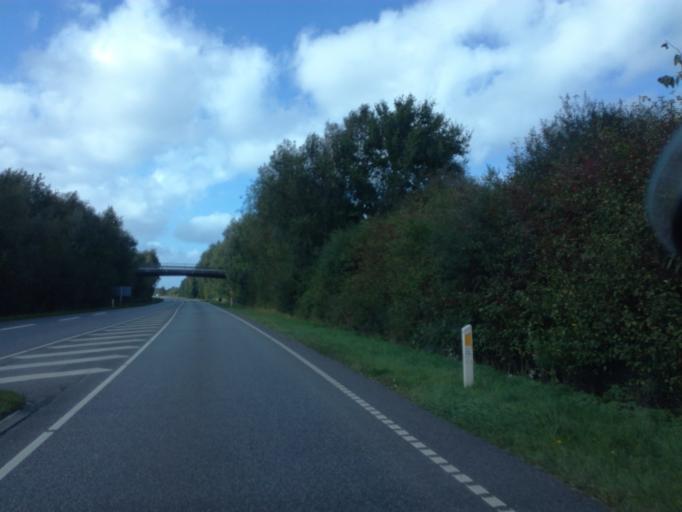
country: DK
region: South Denmark
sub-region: Fredericia Kommune
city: Fredericia
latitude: 55.6248
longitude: 9.7325
